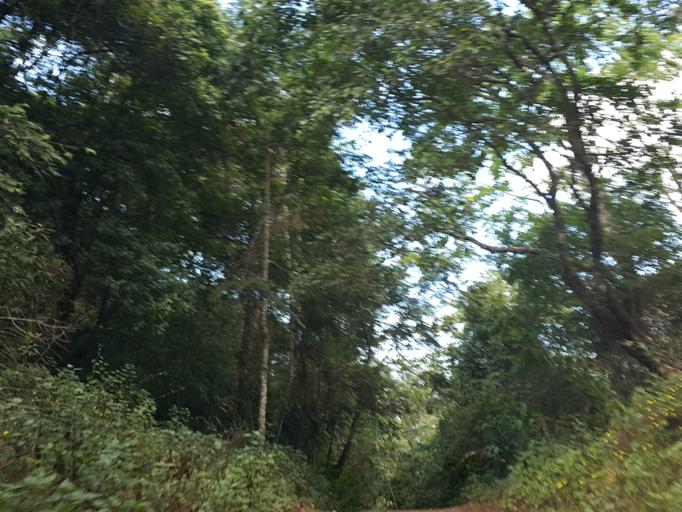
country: TH
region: Chiang Mai
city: Wiang Haeng
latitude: 19.5550
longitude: 98.8138
